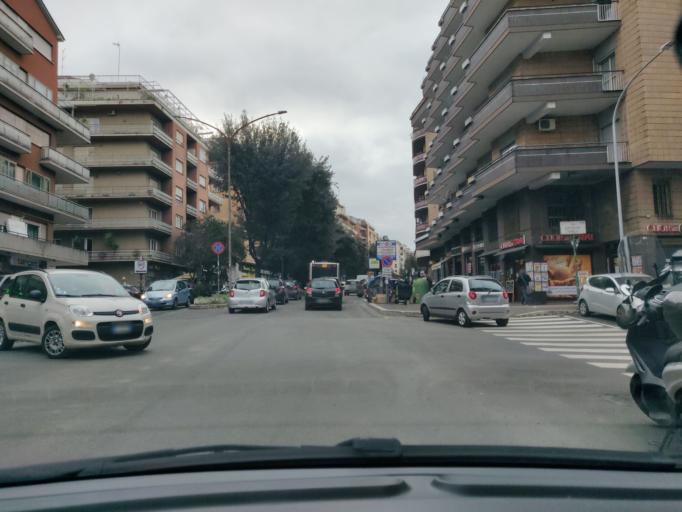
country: VA
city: Vatican City
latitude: 41.8999
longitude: 12.4364
